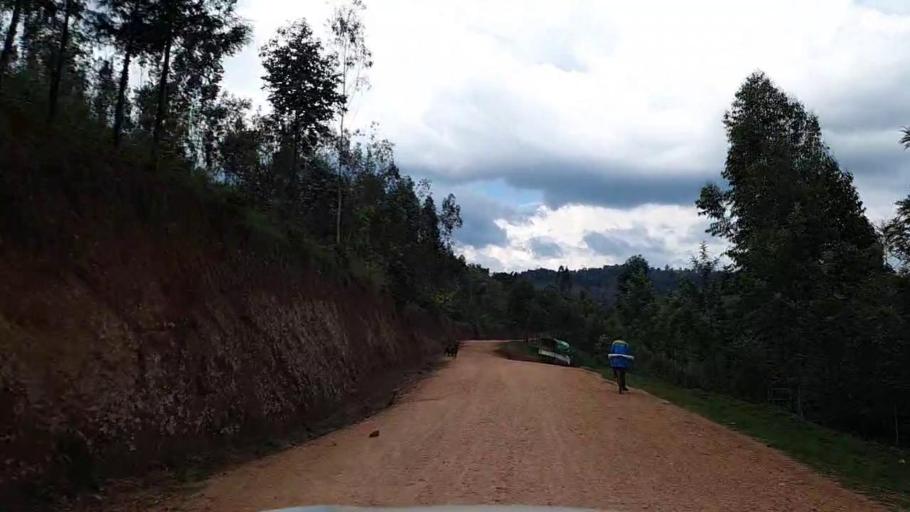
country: RW
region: Southern Province
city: Nyanza
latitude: -2.3934
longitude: 29.6814
